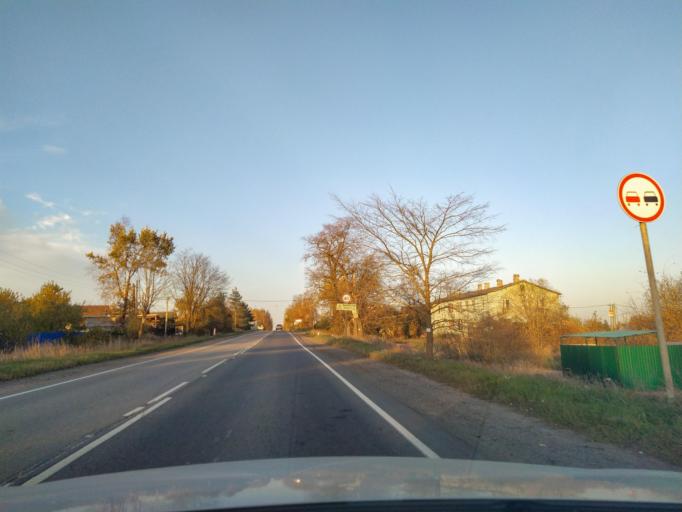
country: RU
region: Leningrad
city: Maloye Verevo
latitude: 59.6093
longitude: 30.1944
